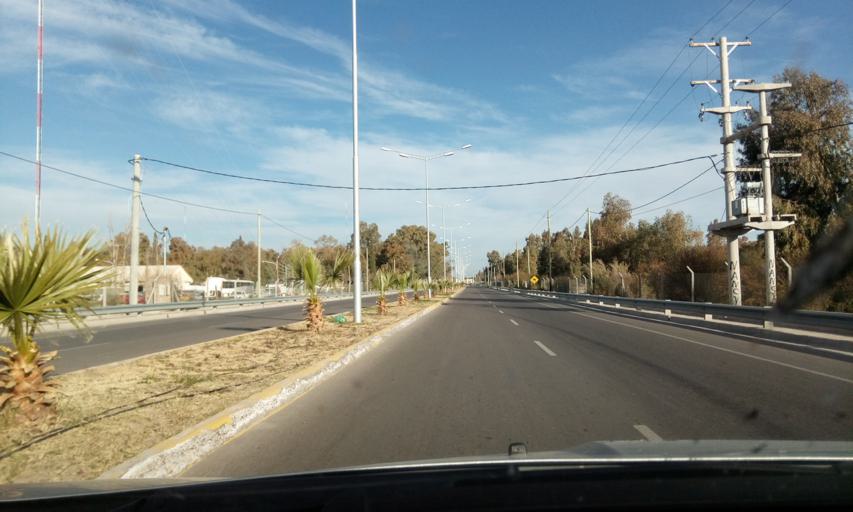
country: AR
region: San Juan
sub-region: Departamento de Rivadavia
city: Rivadavia
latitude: -31.5171
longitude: -68.6304
